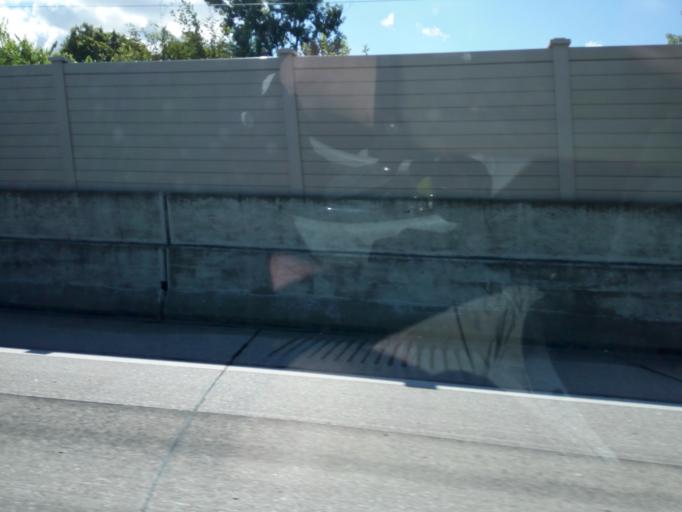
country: US
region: Kentucky
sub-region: Jefferson County
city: Saint Regis Park
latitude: 38.2364
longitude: -85.6208
